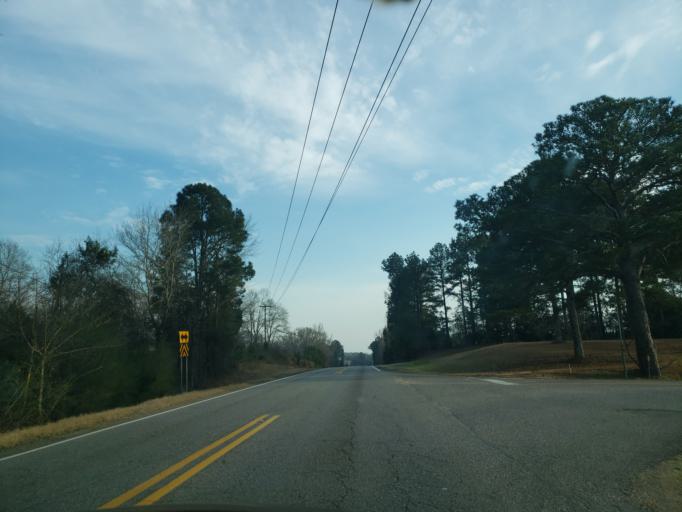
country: US
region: Alabama
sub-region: Hale County
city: Moundville
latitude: 32.9655
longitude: -87.6251
